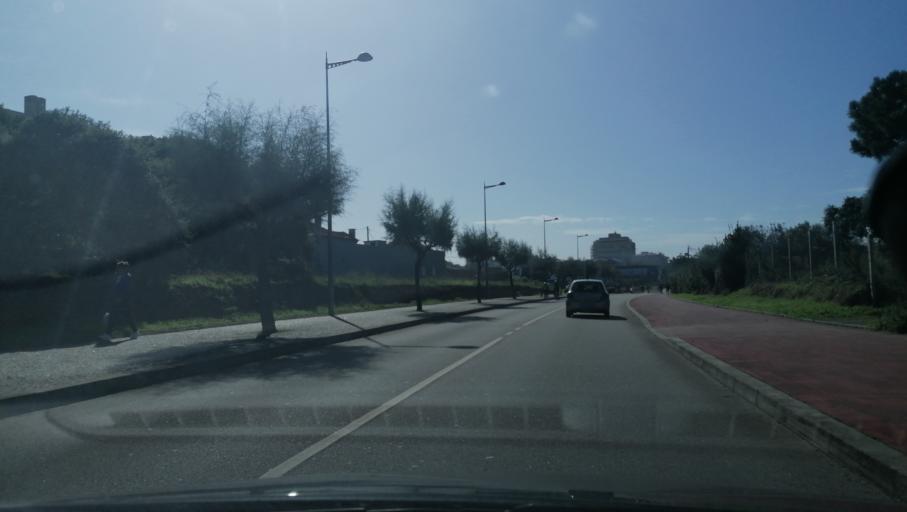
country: PT
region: Aveiro
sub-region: Espinho
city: Espinho
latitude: 41.0169
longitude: -8.6399
